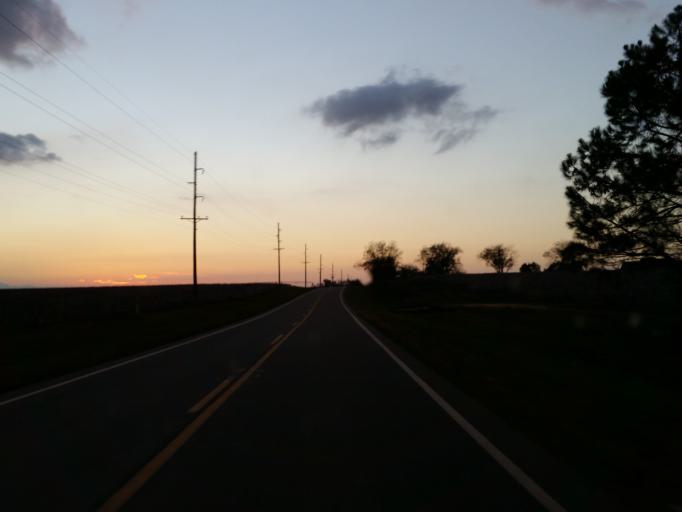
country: US
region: Georgia
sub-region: Dooly County
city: Vienna
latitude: 32.1234
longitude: -83.7359
